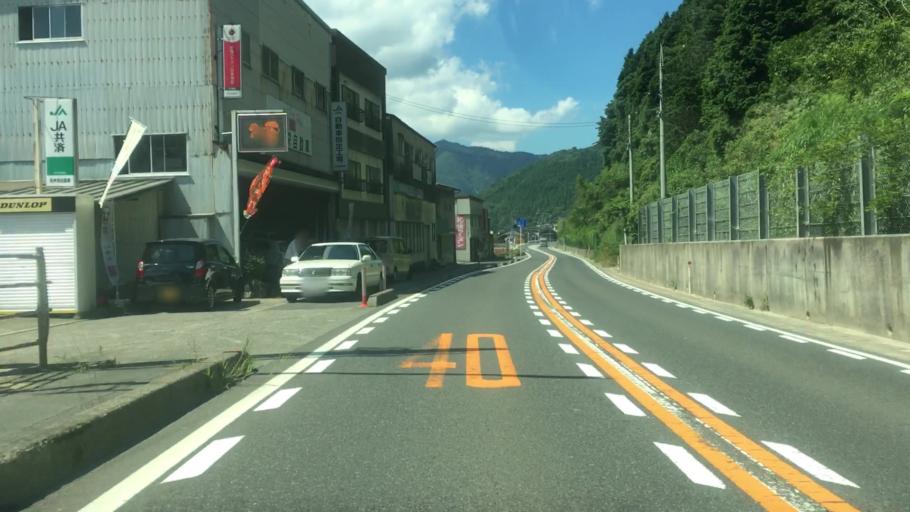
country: JP
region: Tottori
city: Tottori
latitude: 35.2600
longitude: 134.2275
